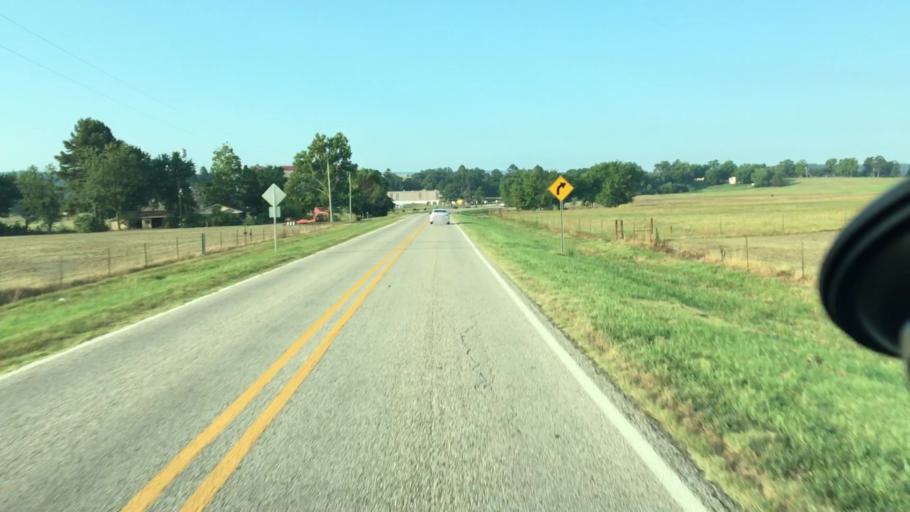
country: US
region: Arkansas
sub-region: Logan County
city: Paris
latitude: 35.3070
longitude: -93.6329
